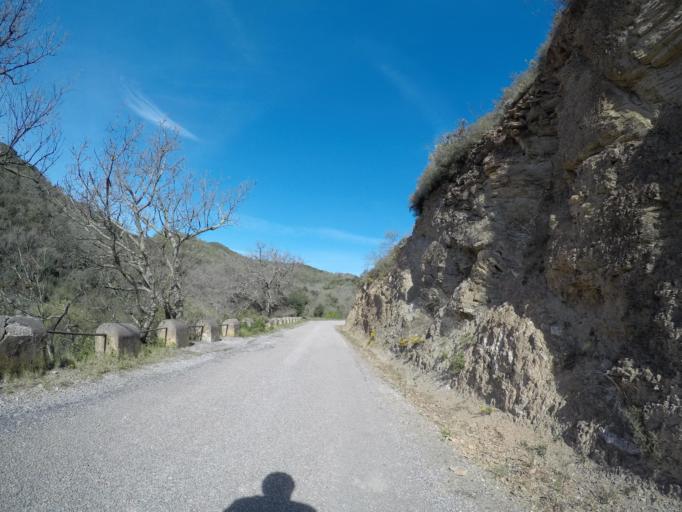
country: FR
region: Languedoc-Roussillon
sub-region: Departement des Pyrenees-Orientales
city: Thuir
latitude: 42.6298
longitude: 2.7018
